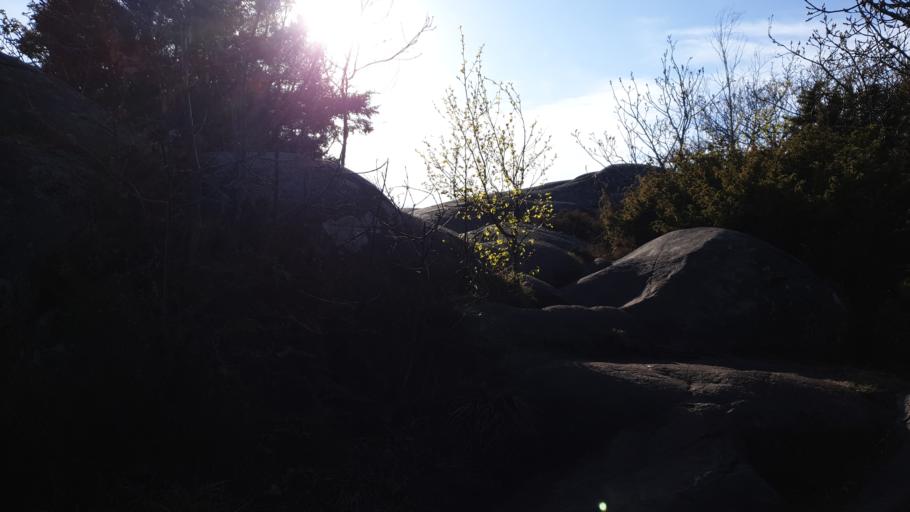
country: SE
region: Vaestra Goetaland
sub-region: Goteborg
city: Billdal
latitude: 57.5908
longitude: 11.9069
